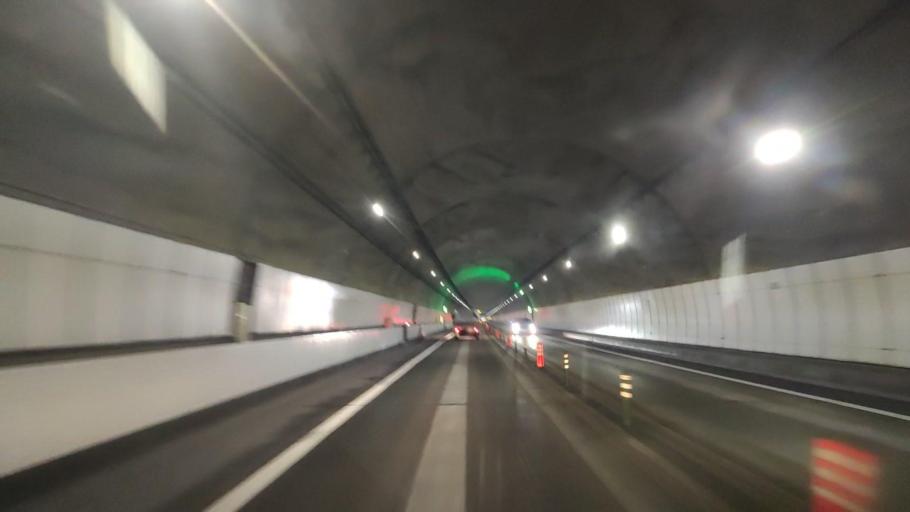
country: JP
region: Gifu
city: Takayama
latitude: 36.1930
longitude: 137.5747
